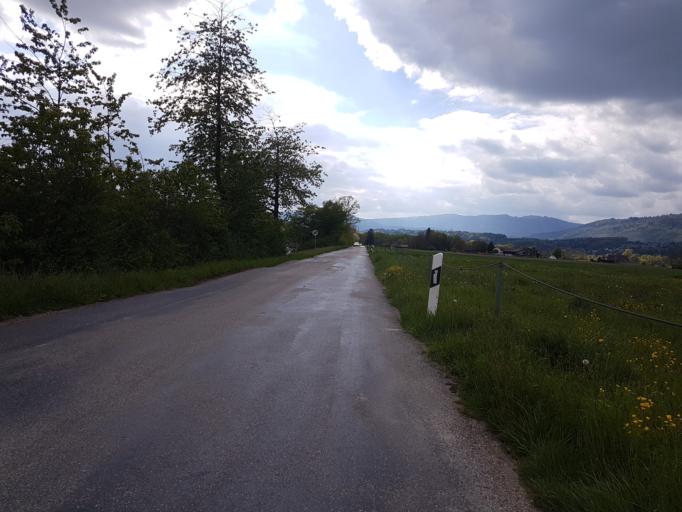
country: CH
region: Bern
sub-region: Biel/Bienne District
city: Meinisberg
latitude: 47.1430
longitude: 7.3529
